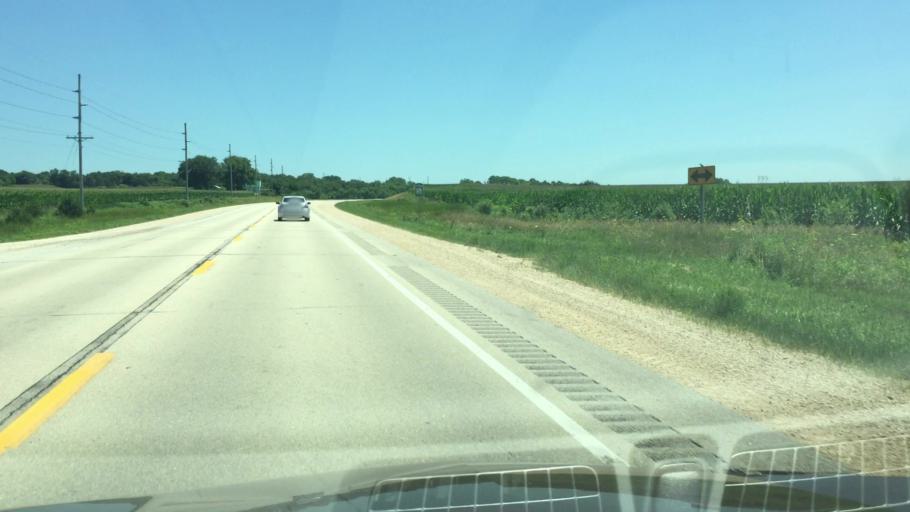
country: US
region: Iowa
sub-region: Jackson County
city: Maquoketa
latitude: 42.0650
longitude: -90.7675
